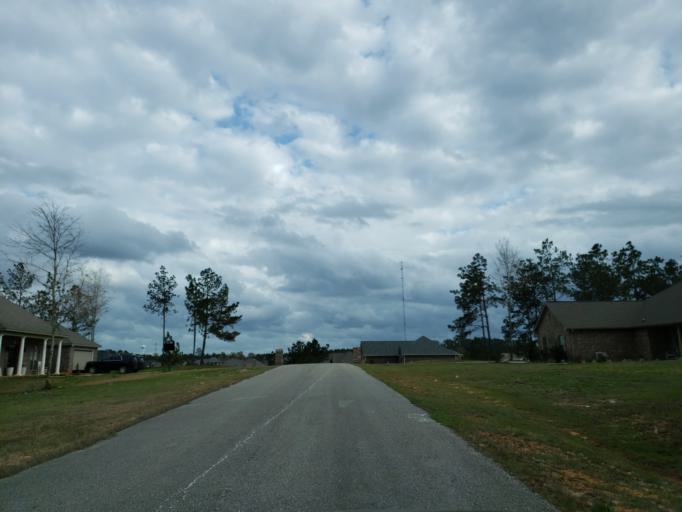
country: US
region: Mississippi
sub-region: Jones County
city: Ellisville
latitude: 31.5540
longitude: -89.2589
